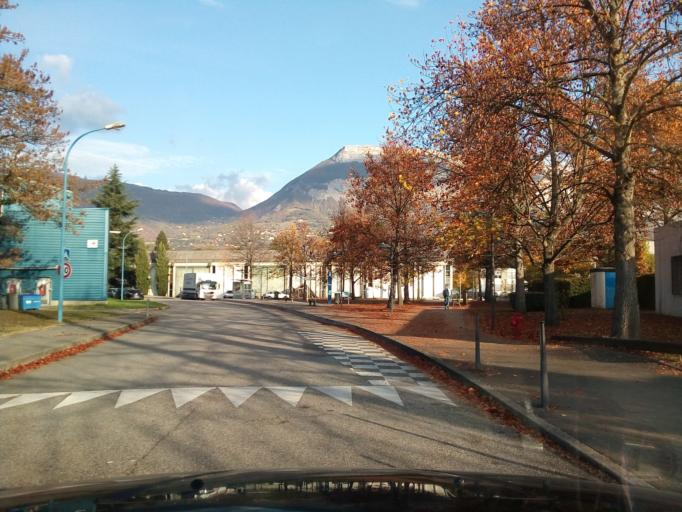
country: FR
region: Rhone-Alpes
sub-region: Departement de l'Isere
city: Corenc
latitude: 45.1971
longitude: 5.7764
